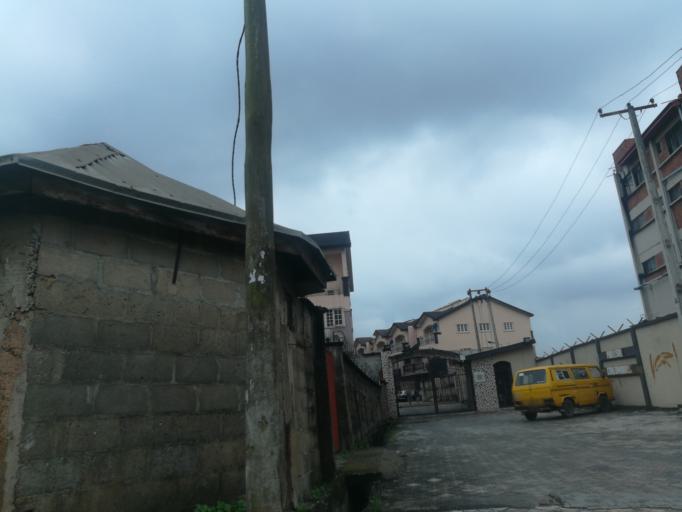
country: NG
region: Lagos
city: Ojota
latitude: 6.5743
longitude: 3.3750
